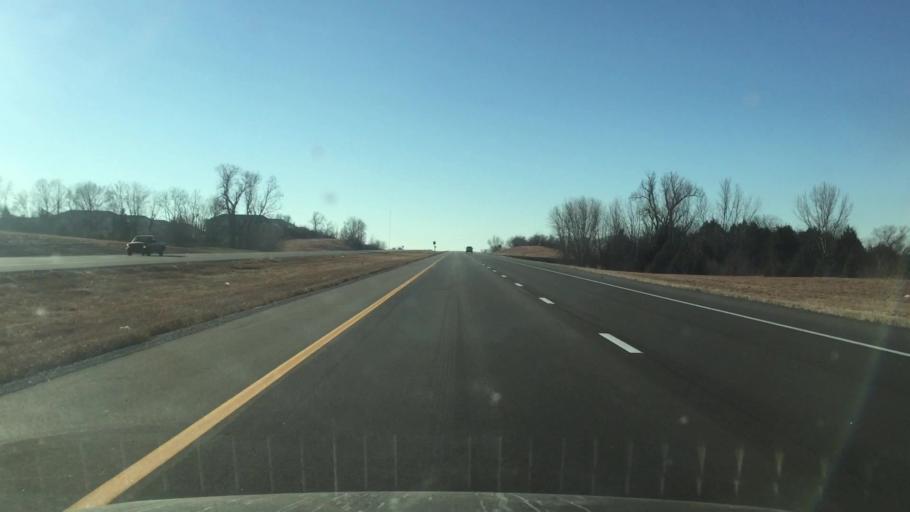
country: US
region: Kansas
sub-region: Johnson County
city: Spring Hill
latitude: 38.7480
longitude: -94.8394
